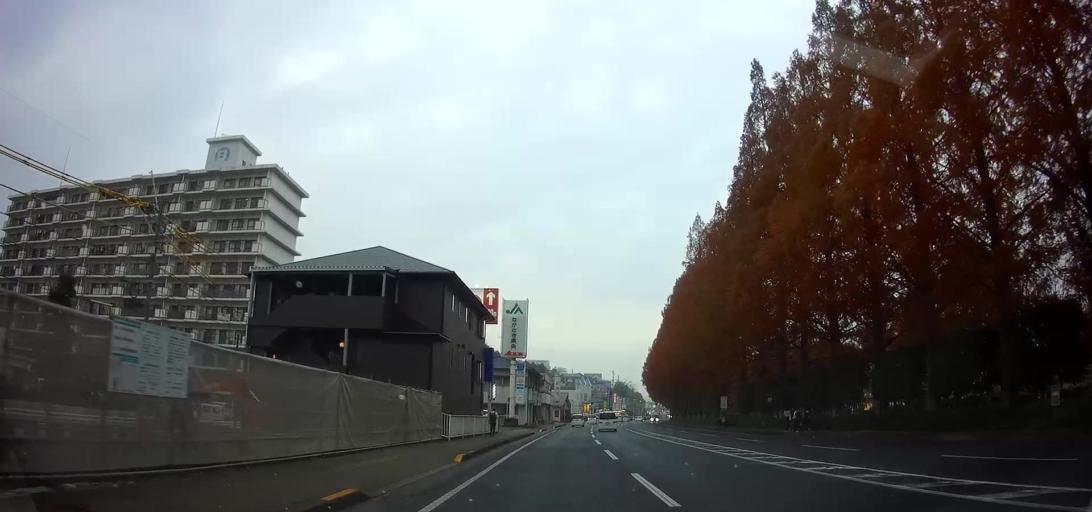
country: JP
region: Nagasaki
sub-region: Isahaya-shi
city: Isahaya
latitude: 32.8344
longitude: 130.0418
